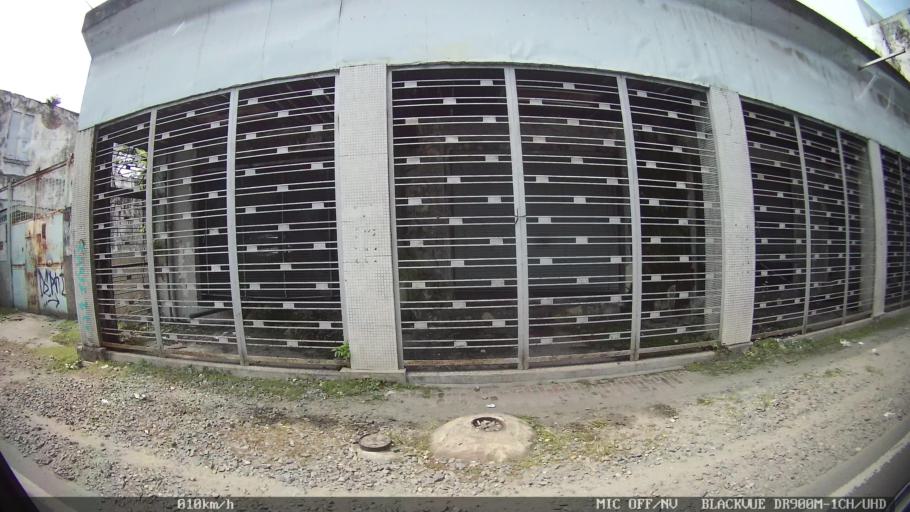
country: ID
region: North Sumatra
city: Medan
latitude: 3.5871
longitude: 98.6761
